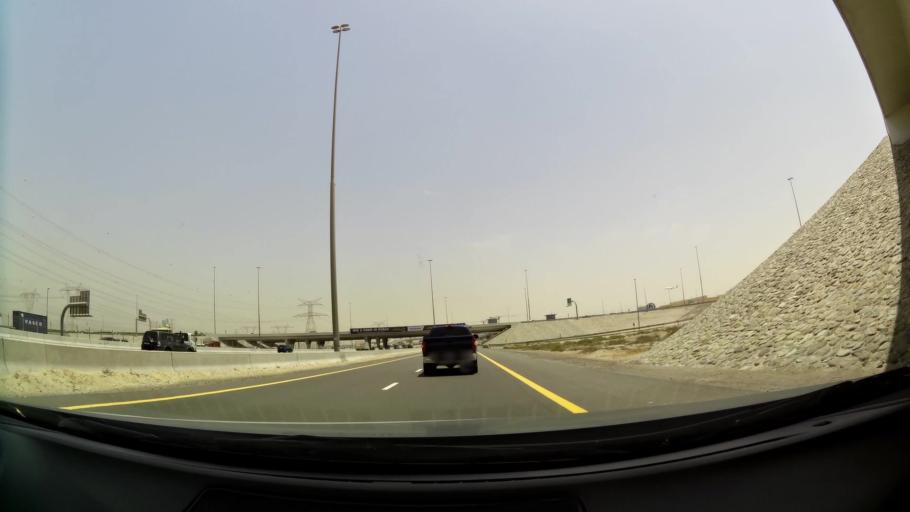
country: AE
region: Ash Shariqah
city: Sharjah
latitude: 25.2106
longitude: 55.4023
